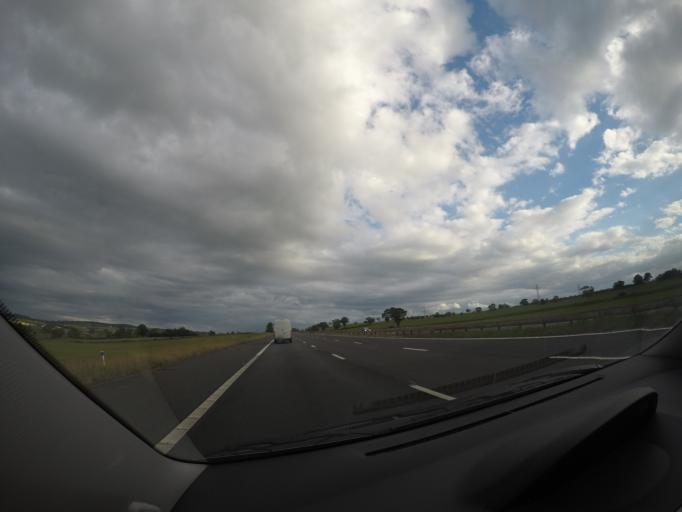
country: GB
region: England
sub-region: Cumbria
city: Penrith
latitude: 54.7084
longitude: -2.7931
